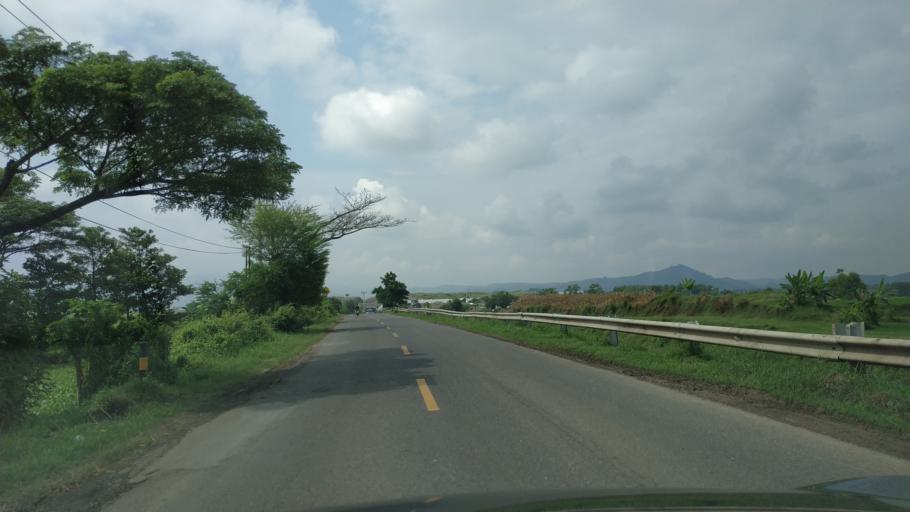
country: ID
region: Central Java
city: Margasari
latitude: -7.0834
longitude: 108.9829
